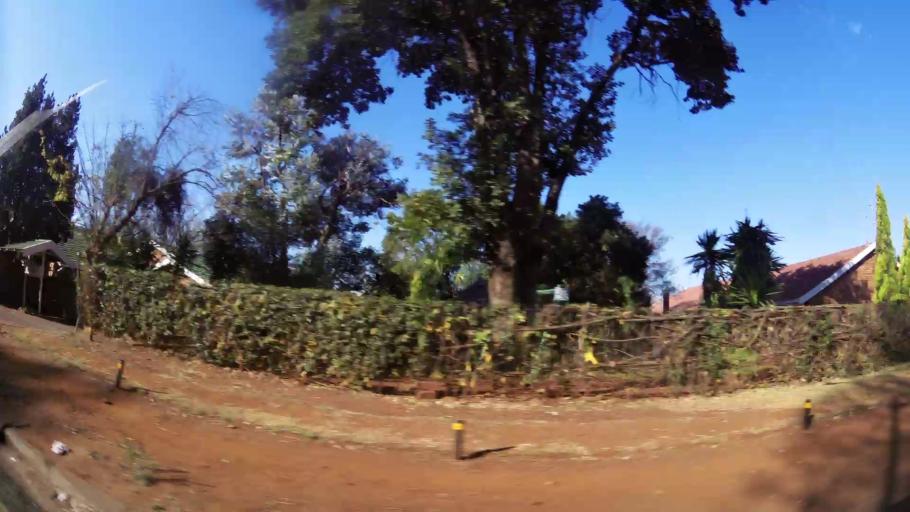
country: ZA
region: Gauteng
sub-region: City of Tshwane Metropolitan Municipality
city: Centurion
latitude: -25.8574
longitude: 28.1670
